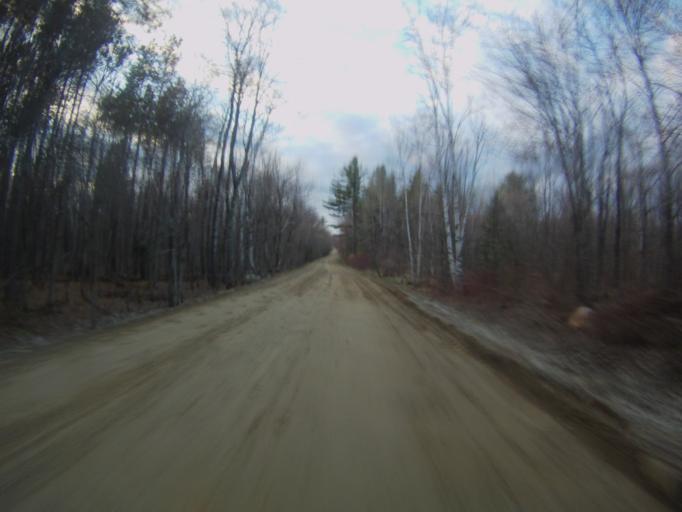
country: US
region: Vermont
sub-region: Rutland County
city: Brandon
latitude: 43.9028
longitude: -73.0154
